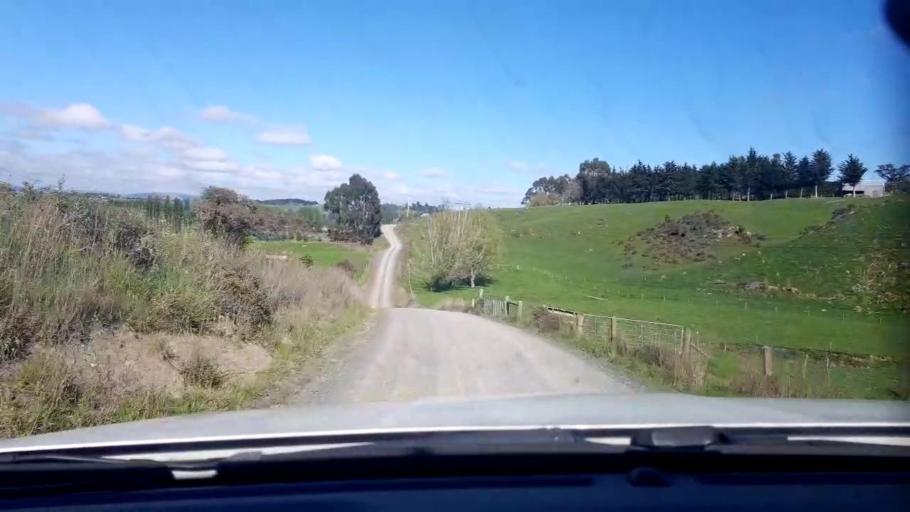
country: NZ
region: Otago
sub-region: Clutha District
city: Balclutha
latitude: -46.2231
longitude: 169.7403
